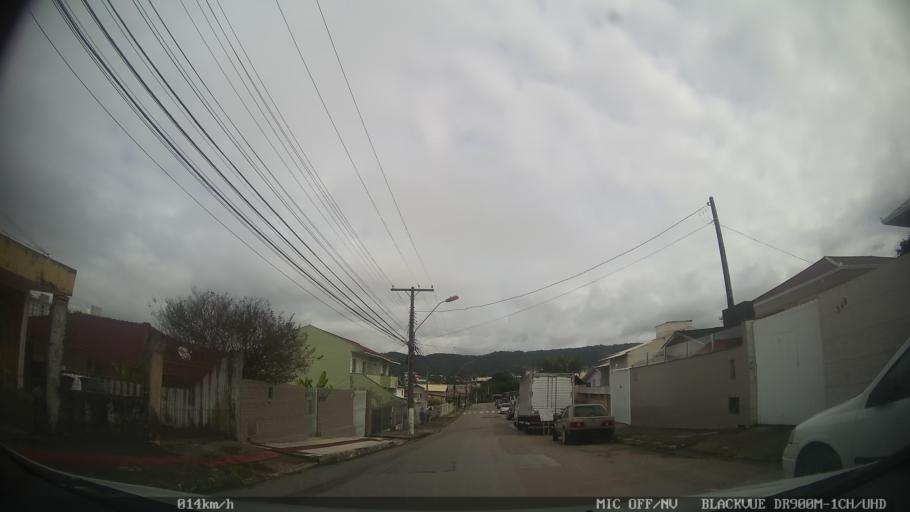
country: BR
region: Santa Catarina
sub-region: Biguacu
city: Biguacu
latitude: -27.5385
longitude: -48.6325
